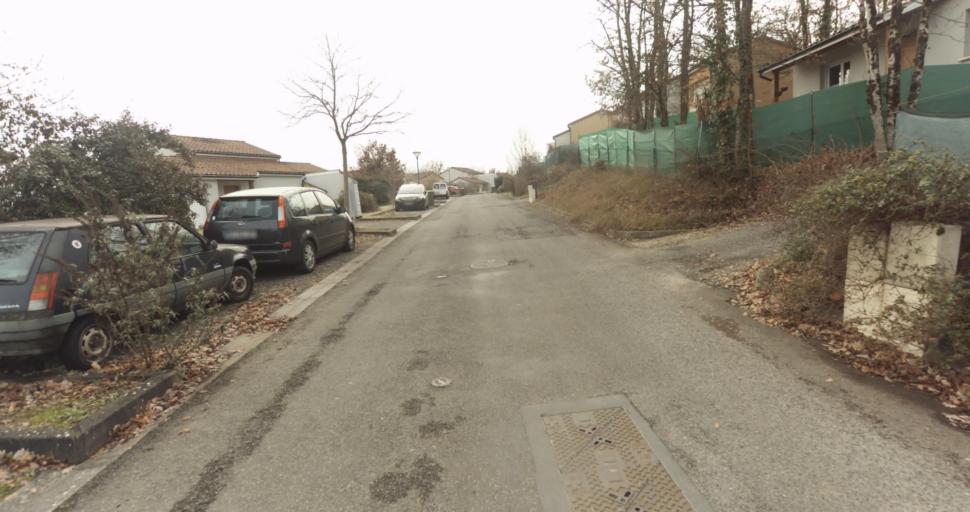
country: FR
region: Midi-Pyrenees
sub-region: Departement du Lot
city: Figeac
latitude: 44.6111
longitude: 2.0104
